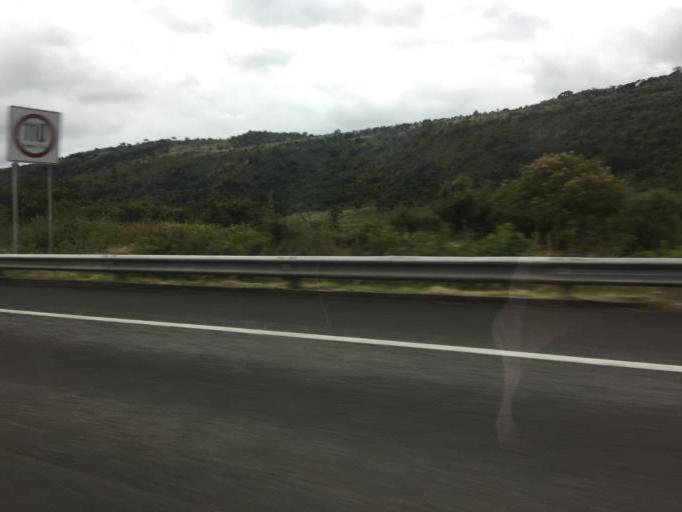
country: MX
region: Jalisco
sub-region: Zapotlan del Rey
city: Zapotlan del Rey
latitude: 20.5228
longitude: -102.9950
